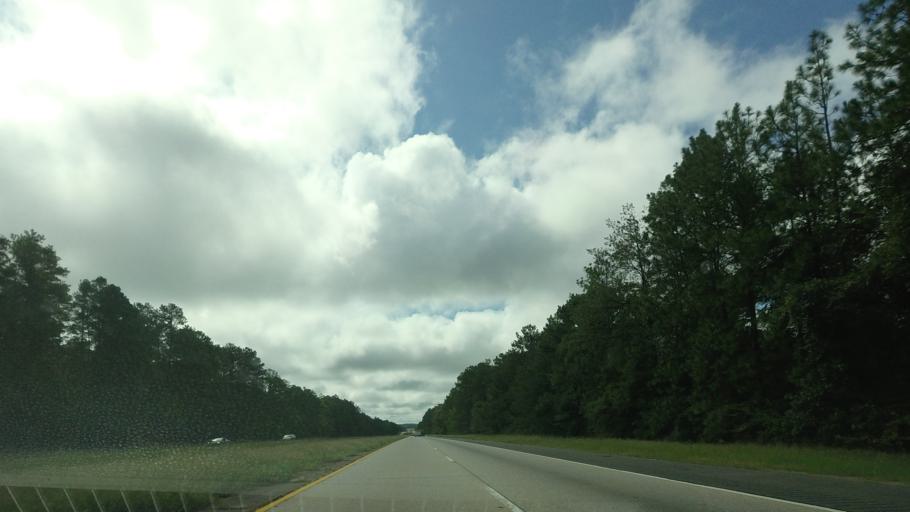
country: US
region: Georgia
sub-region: Bibb County
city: Macon
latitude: 32.7445
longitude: -83.5459
